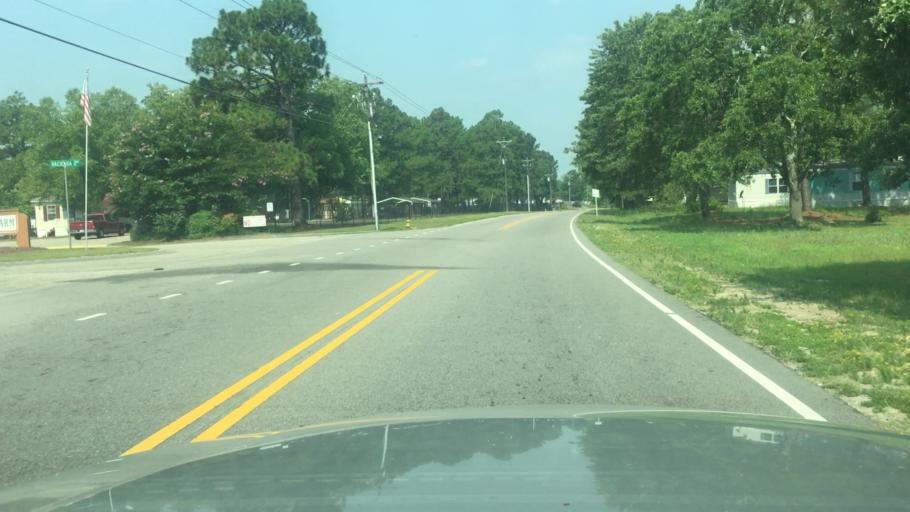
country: US
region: North Carolina
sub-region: Cumberland County
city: Hope Mills
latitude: 35.0003
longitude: -78.9518
